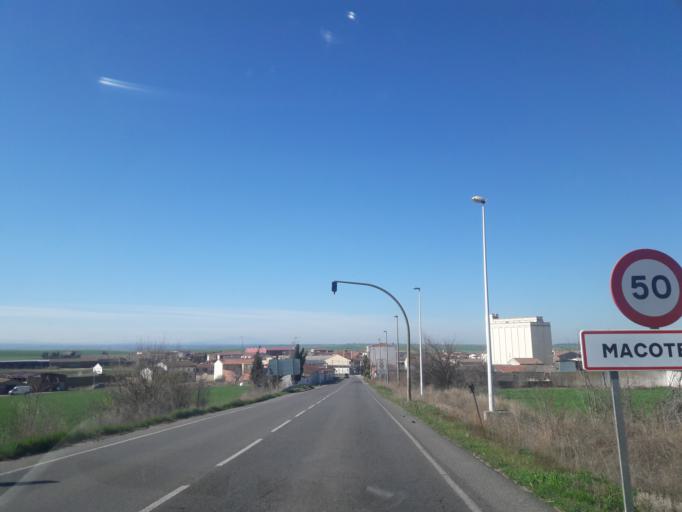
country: ES
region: Castille and Leon
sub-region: Provincia de Salamanca
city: Macotera
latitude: 40.8323
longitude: -5.2773
